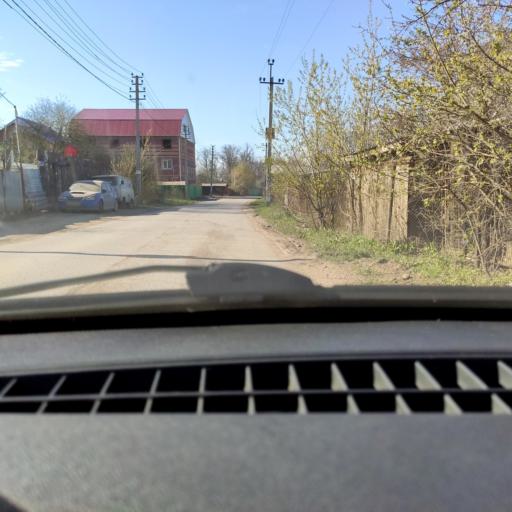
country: RU
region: Bashkortostan
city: Ufa
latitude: 54.6965
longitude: 55.9013
